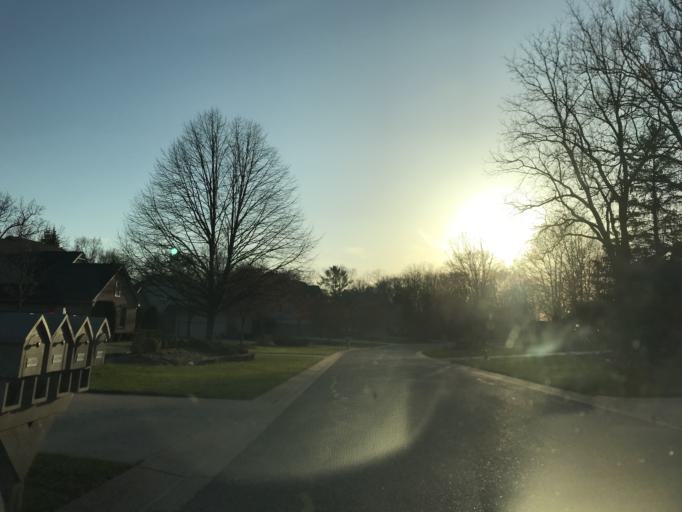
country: US
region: Michigan
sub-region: Oakland County
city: South Lyon
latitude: 42.4554
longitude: -83.5820
